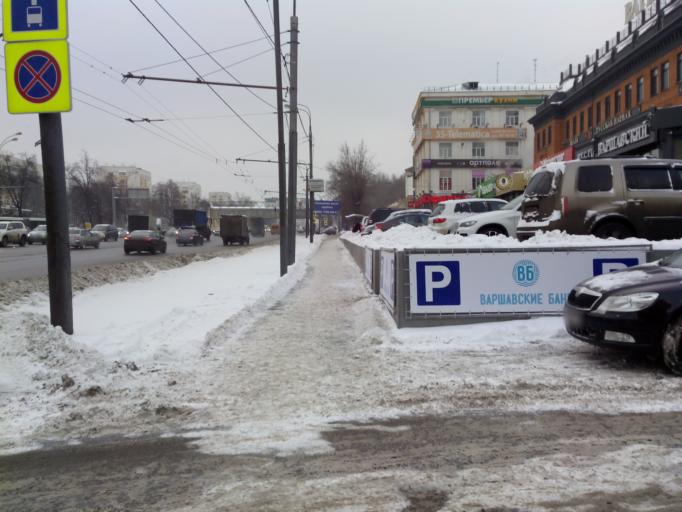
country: RU
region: Moscow
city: Kotlovka
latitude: 55.6808
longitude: 37.6239
